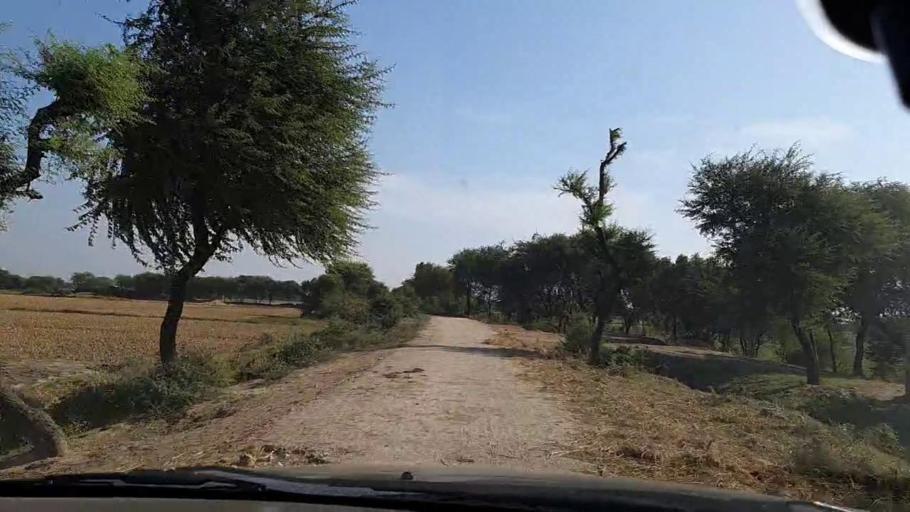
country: PK
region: Sindh
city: Mirpur Batoro
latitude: 24.6322
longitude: 68.2633
